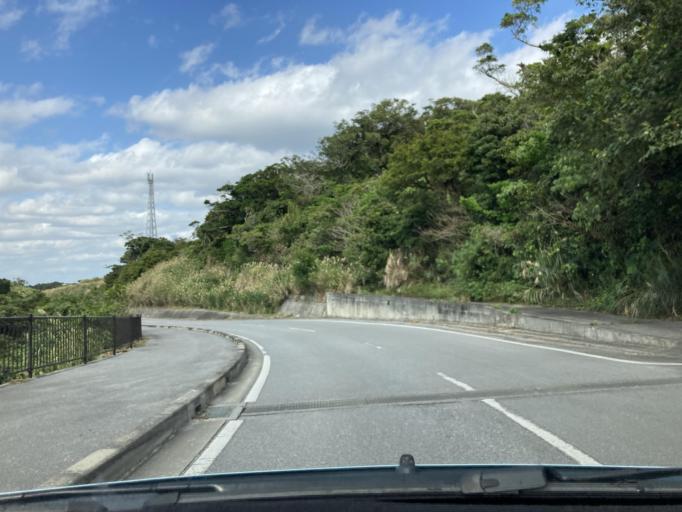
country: JP
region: Okinawa
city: Tomigusuku
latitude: 26.1719
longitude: 127.7601
